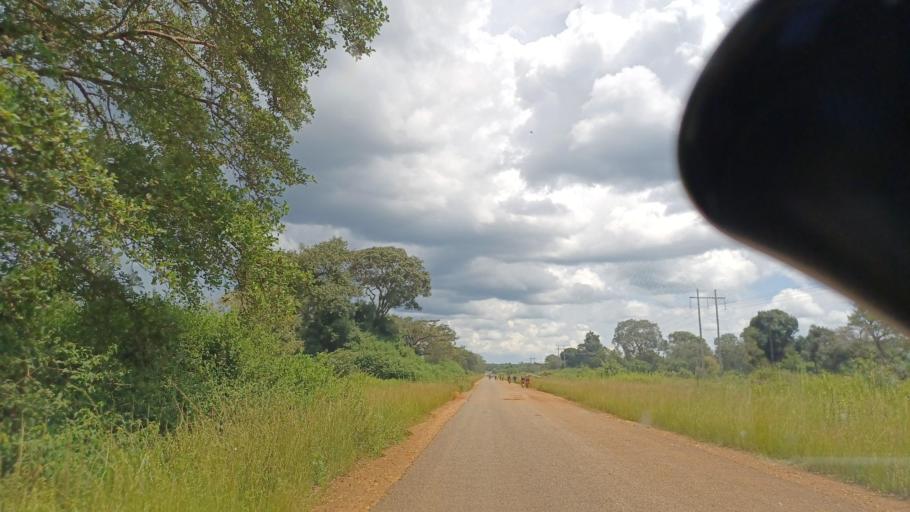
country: ZM
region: North-Western
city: Solwezi
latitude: -12.7690
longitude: 26.0161
